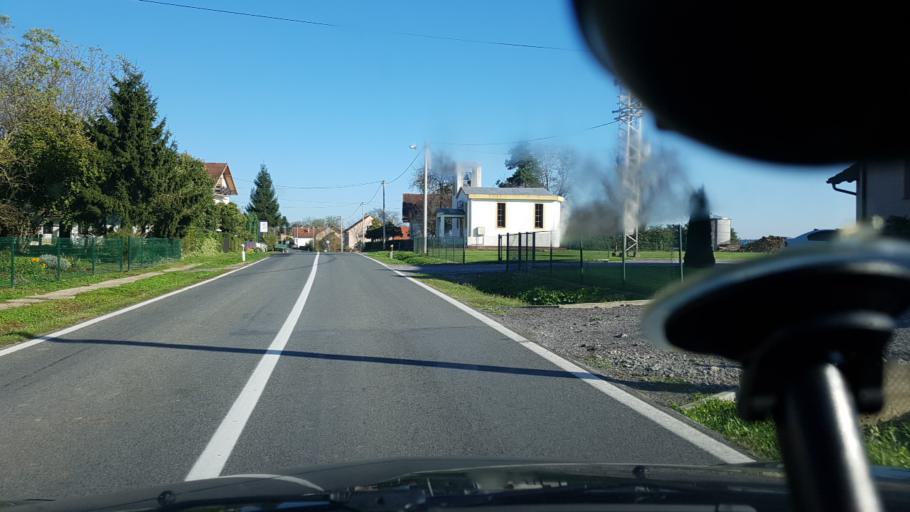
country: HR
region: Bjelovarsko-Bilogorska
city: Gudovac
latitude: 45.8330
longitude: 16.7894
